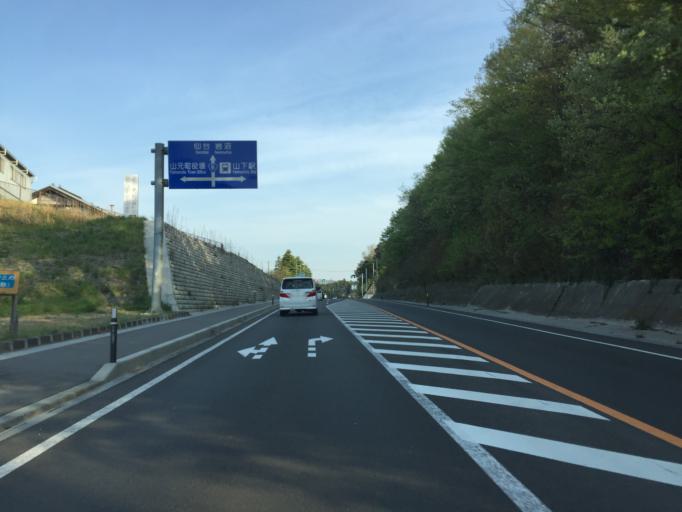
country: JP
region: Miyagi
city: Watari
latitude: 37.9618
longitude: 140.8804
